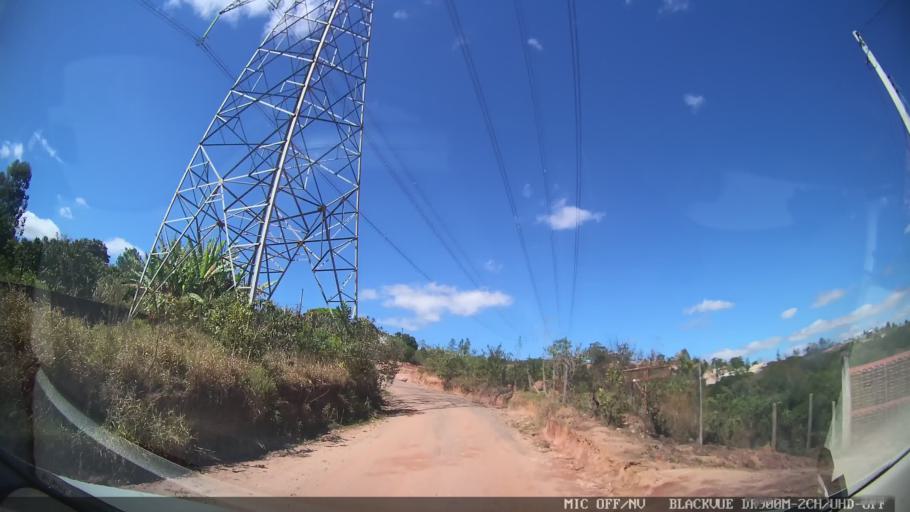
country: BR
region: Sao Paulo
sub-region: Jarinu
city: Jarinu
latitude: -23.1604
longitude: -46.7129
